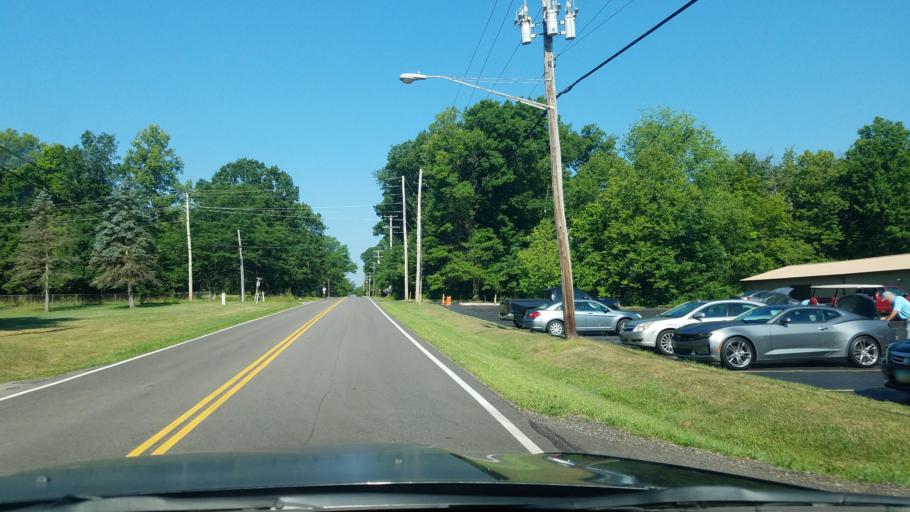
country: US
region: Ohio
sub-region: Trumbull County
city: Champion Heights
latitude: 41.2916
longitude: -80.8291
